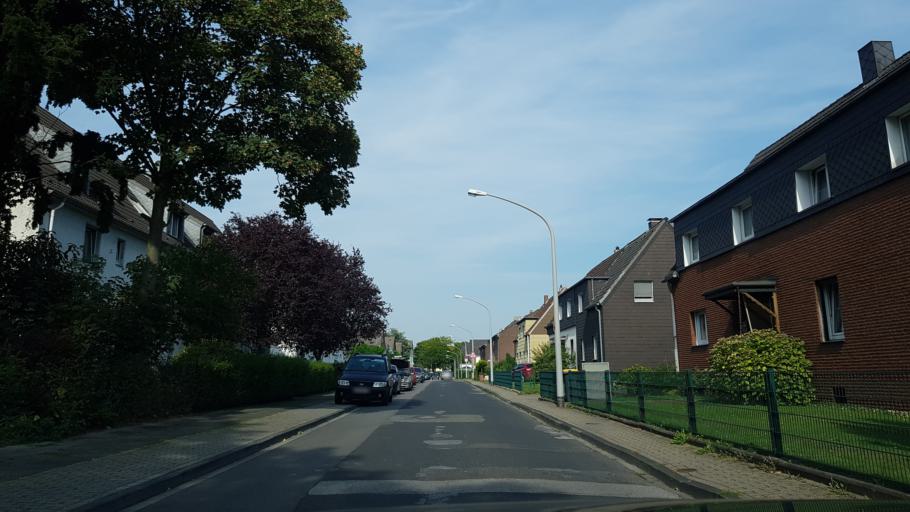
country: DE
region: North Rhine-Westphalia
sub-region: Regierungsbezirk Dusseldorf
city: Hochfeld
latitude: 51.3762
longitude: 6.7636
